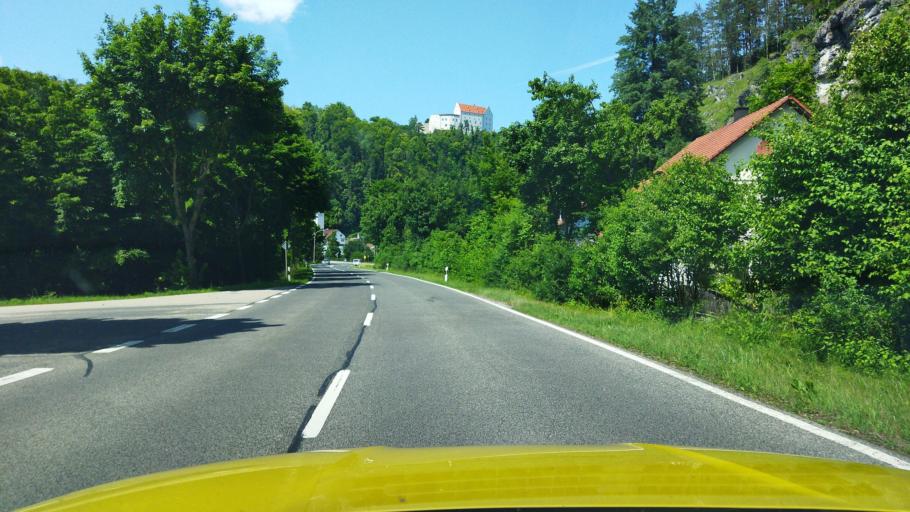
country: DE
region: Bavaria
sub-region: Lower Bavaria
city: Riedenburg
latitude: 48.9558
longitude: 11.6825
